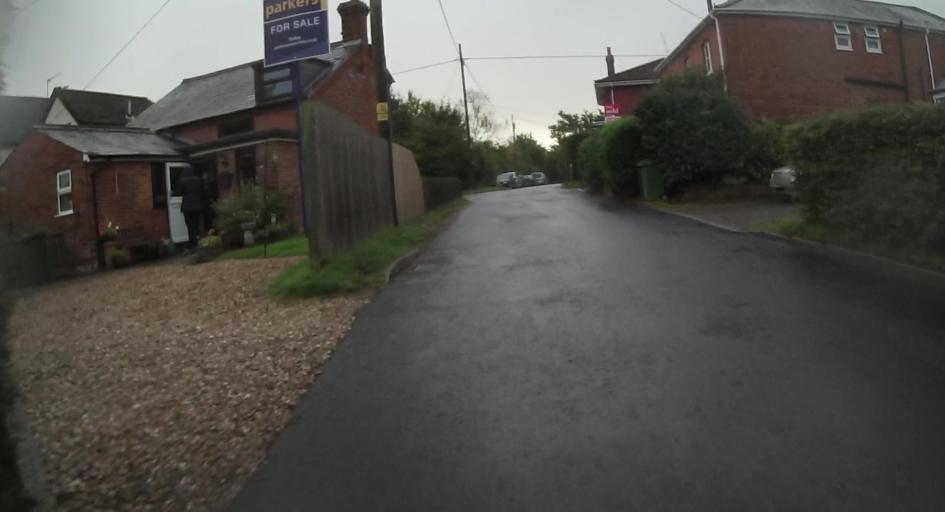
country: GB
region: England
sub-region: Hampshire
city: Tadley
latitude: 51.3155
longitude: -1.1465
